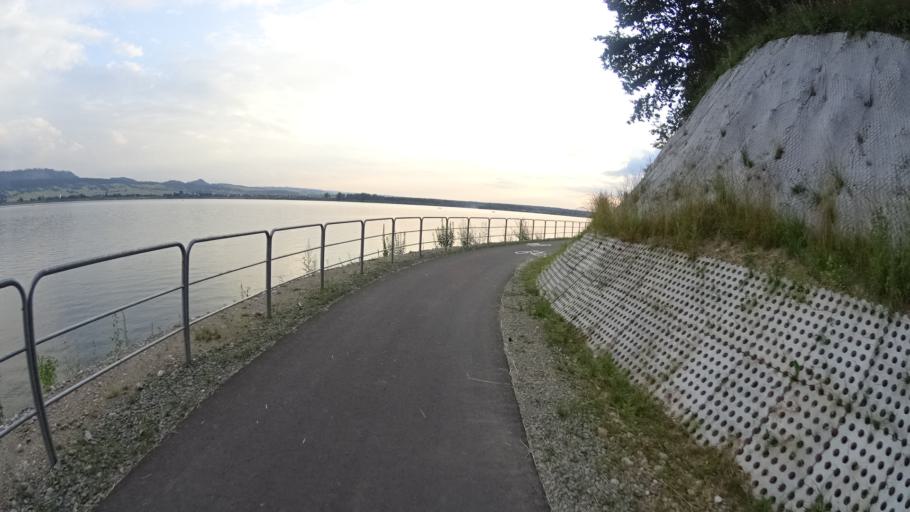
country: PL
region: Lesser Poland Voivodeship
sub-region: Powiat nowotarski
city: Frydman
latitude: 49.4636
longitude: 20.2413
